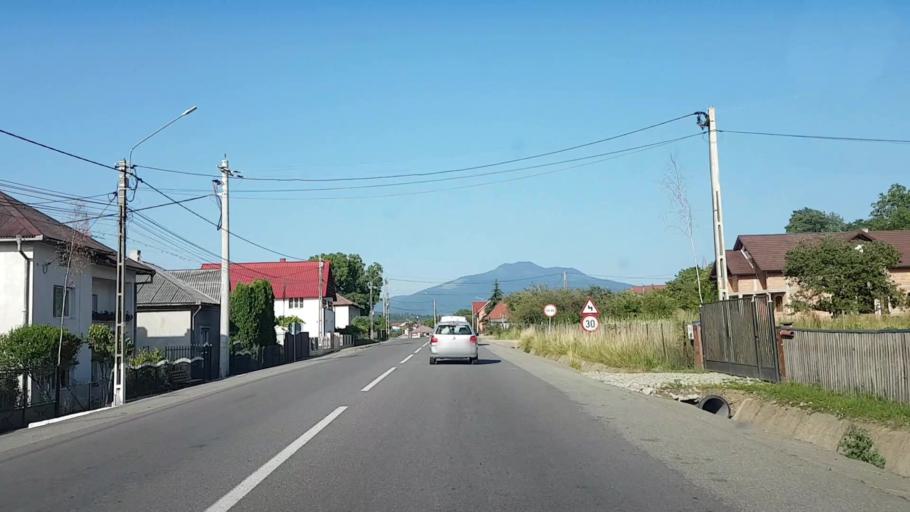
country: RO
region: Bistrita-Nasaud
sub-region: Comuna Prundu Bargaului
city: Susenii Bargaului
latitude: 47.2170
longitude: 24.7067
